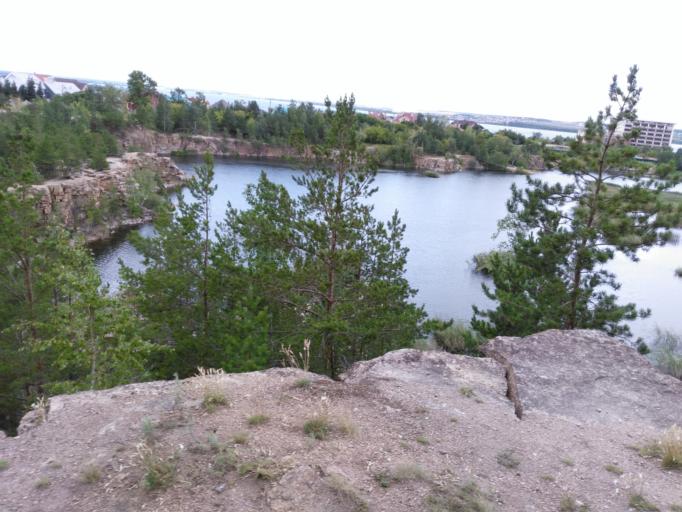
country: RU
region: Chelyabinsk
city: Novosineglazovskiy
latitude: 55.1229
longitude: 61.3387
